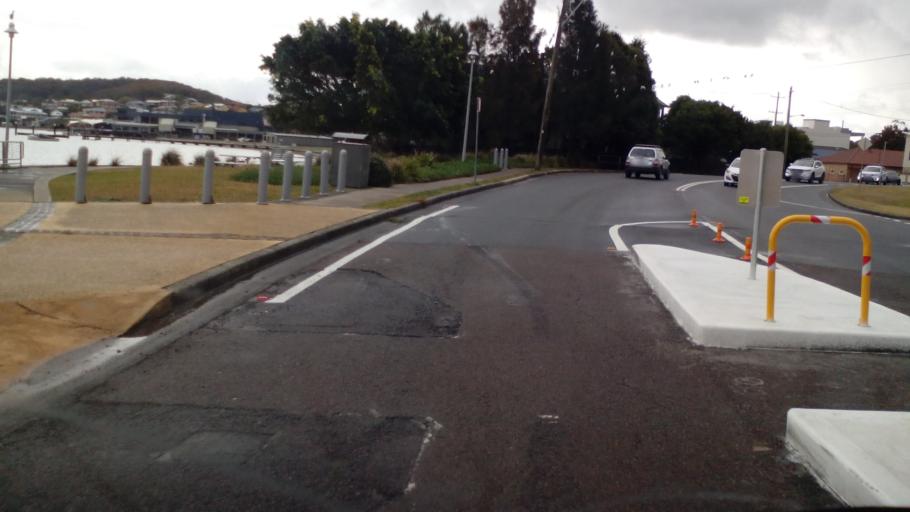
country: AU
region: New South Wales
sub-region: Lake Macquarie Shire
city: Belmont
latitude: -33.0330
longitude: 151.6556
